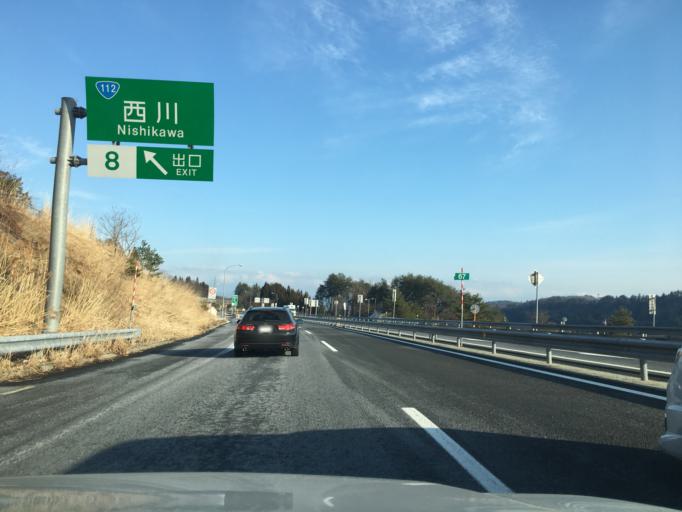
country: JP
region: Yamagata
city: Sagae
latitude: 38.4244
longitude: 140.1637
